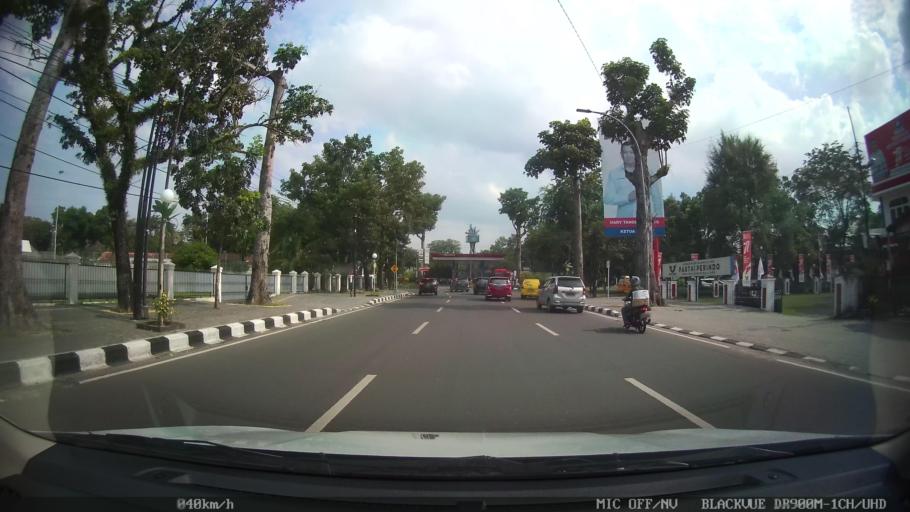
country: ID
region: North Sumatra
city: Medan
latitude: 3.5794
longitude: 98.6768
